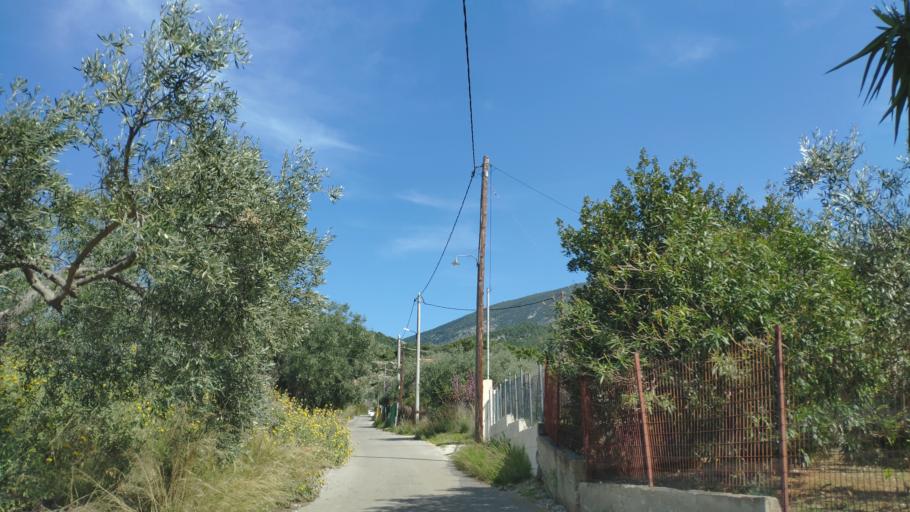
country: GR
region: Central Greece
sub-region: Nomos Voiotias
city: Kaparellion
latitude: 38.1468
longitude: 23.2253
